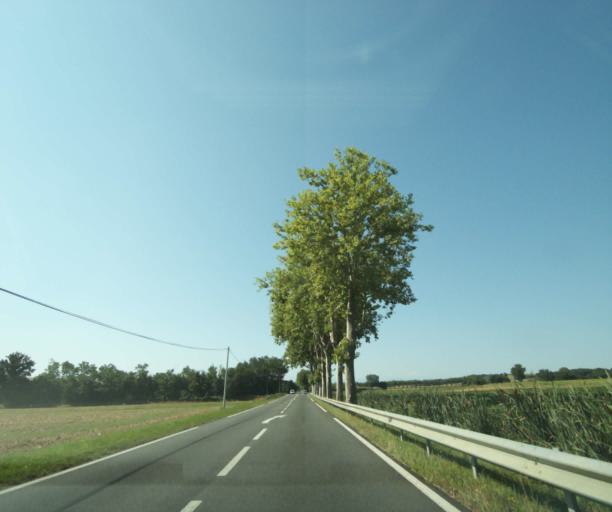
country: FR
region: Midi-Pyrenees
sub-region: Departement de la Haute-Garonne
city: Saint-Sulpice-sur-Leze
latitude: 43.3525
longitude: 1.3259
